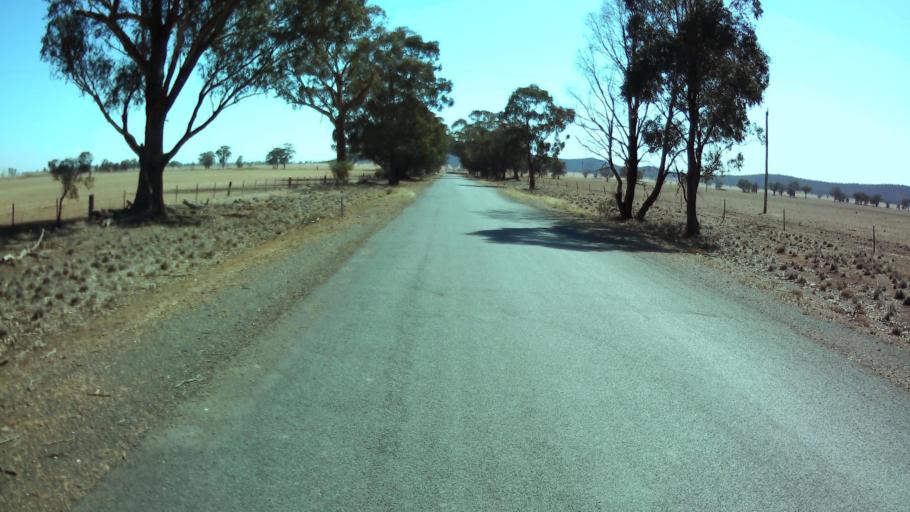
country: AU
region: New South Wales
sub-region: Weddin
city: Grenfell
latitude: -33.7081
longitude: 147.9148
